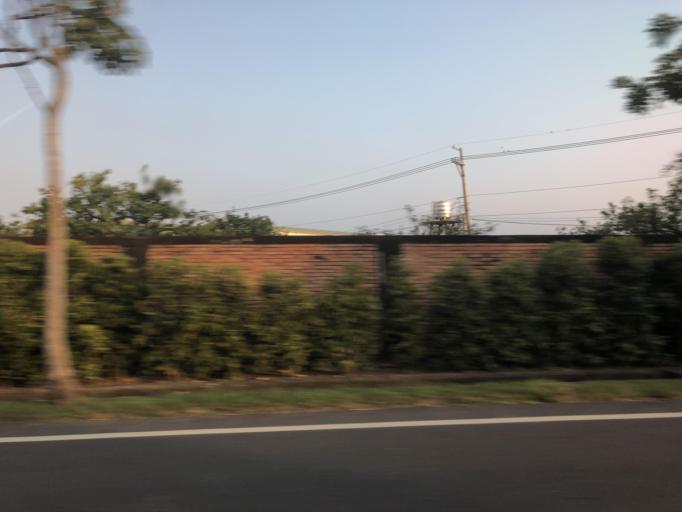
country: TW
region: Taiwan
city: Xinying
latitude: 23.1953
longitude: 120.2632
